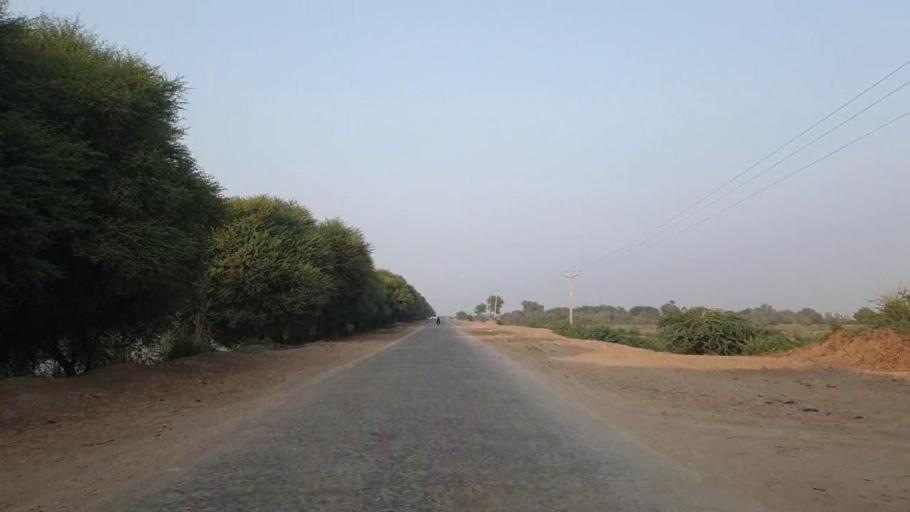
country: PK
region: Sindh
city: Tando Muhammad Khan
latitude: 25.1282
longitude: 68.4325
